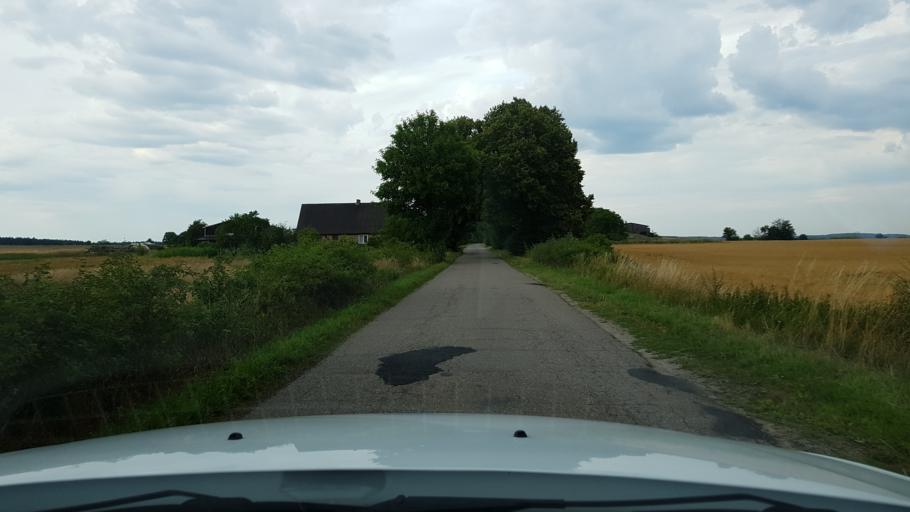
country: PL
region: West Pomeranian Voivodeship
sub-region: Powiat walecki
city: Walcz
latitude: 53.3871
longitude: 16.3262
